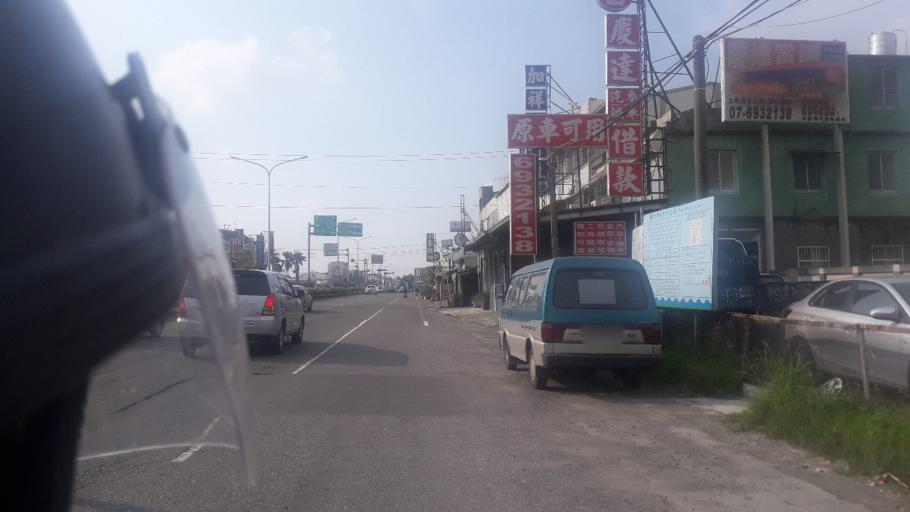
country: TW
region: Taiwan
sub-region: Tainan
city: Tainan
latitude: 22.8790
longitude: 120.2515
